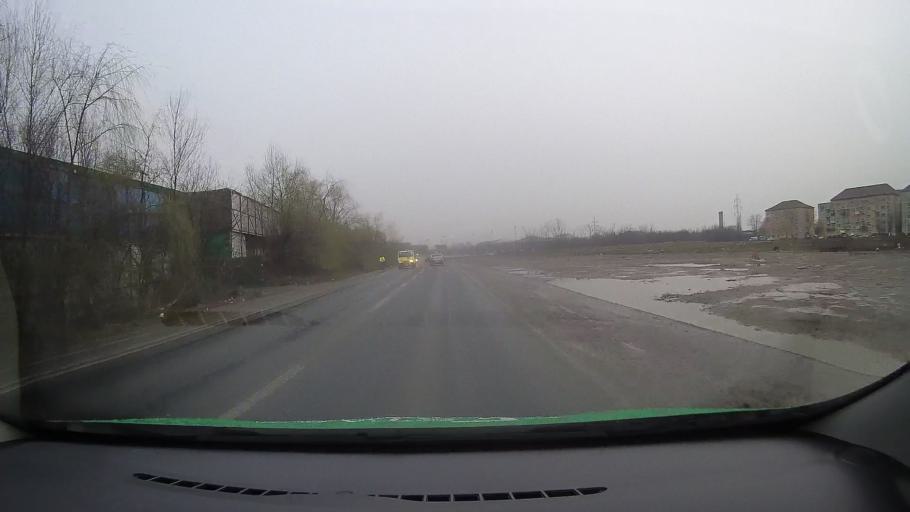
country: RO
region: Timis
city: Timisoara
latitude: 45.7390
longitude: 21.2501
